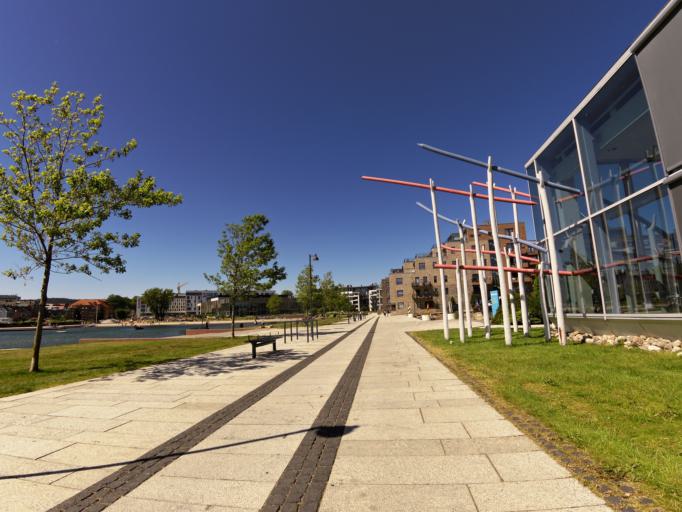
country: NO
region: Vest-Agder
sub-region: Kristiansand
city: Kristiansand
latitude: 58.1448
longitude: 8.0094
